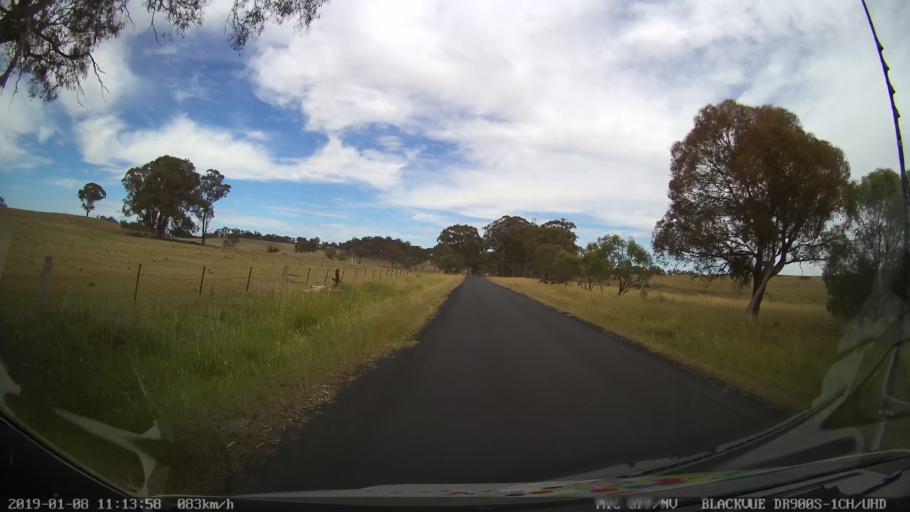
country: AU
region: New South Wales
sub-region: Guyra
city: Guyra
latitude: -30.2287
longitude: 151.5931
